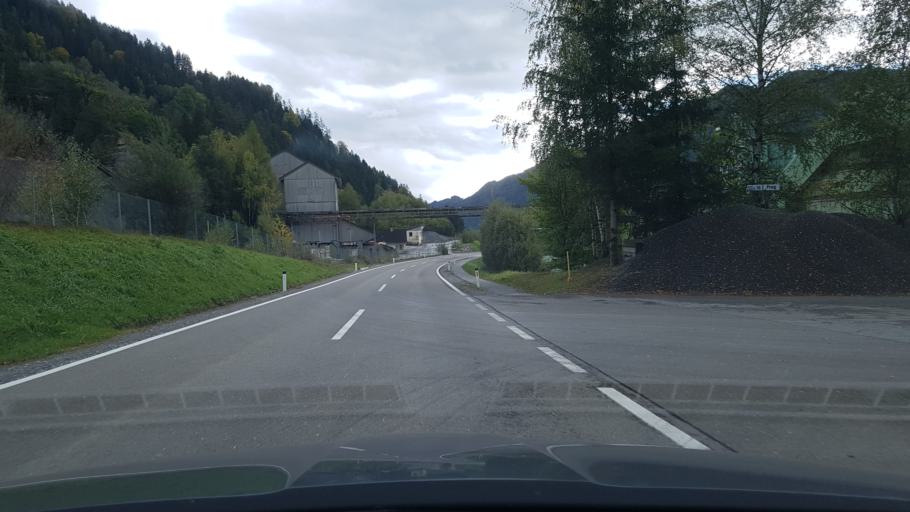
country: AT
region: Styria
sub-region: Politischer Bezirk Murau
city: Oberwolz Stadt
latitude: 47.1478
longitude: 14.2771
